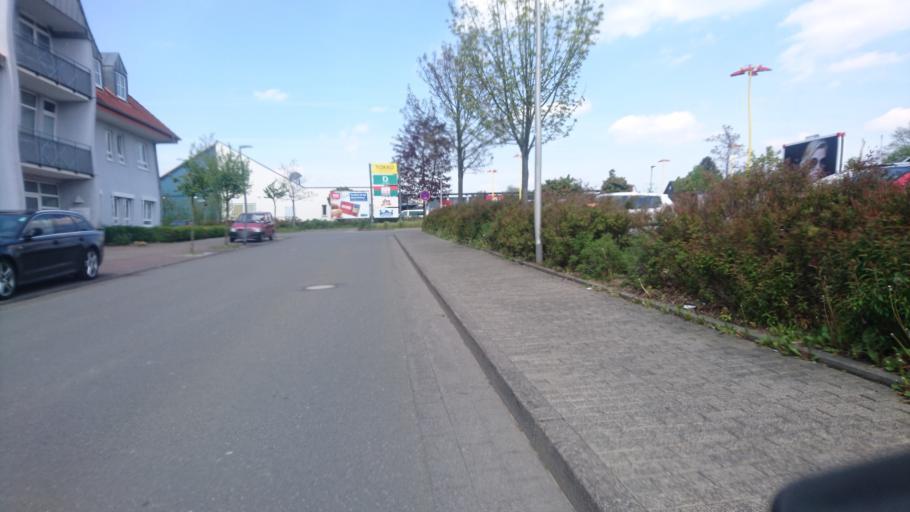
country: DE
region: Hesse
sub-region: Regierungsbezirk Kassel
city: Bad Arolsen
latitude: 51.3815
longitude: 9.0108
